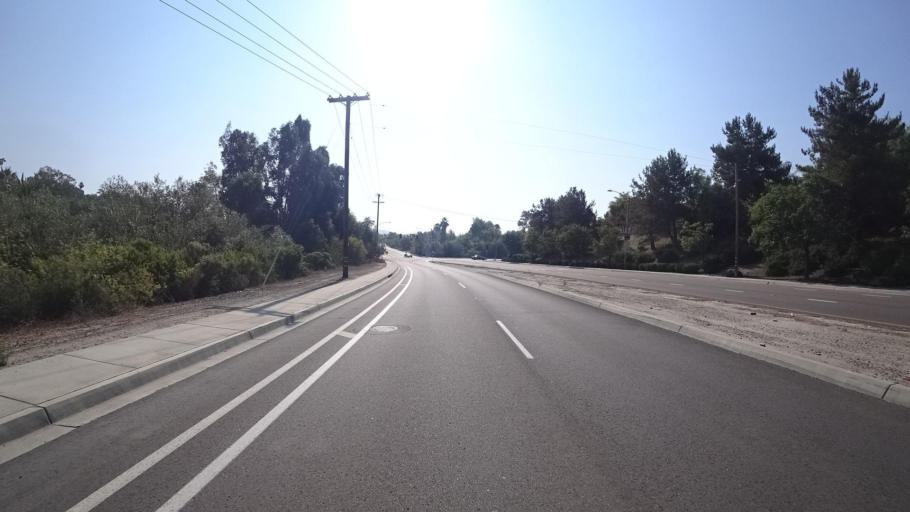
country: US
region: California
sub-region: San Diego County
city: Vista
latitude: 33.2361
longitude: -117.2628
